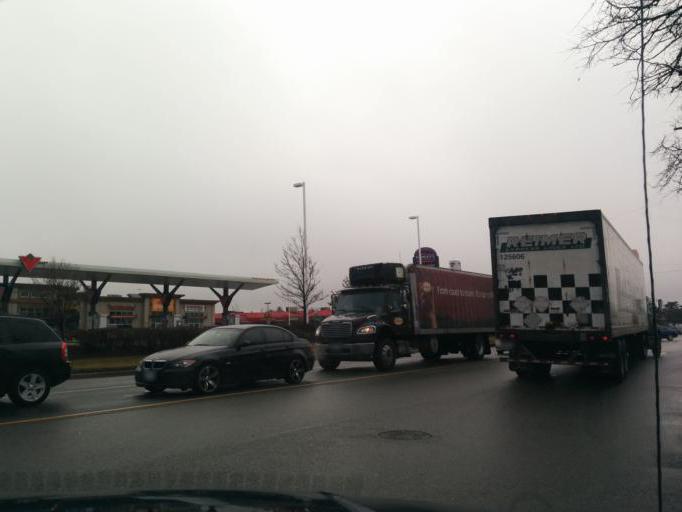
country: CA
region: Ontario
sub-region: Halton
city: Milton
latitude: 43.5240
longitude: -79.9001
